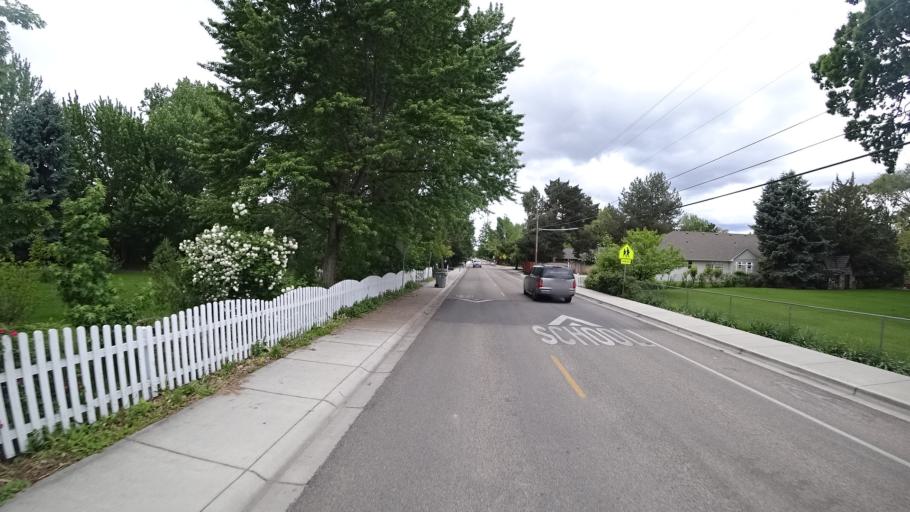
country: US
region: Idaho
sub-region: Ada County
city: Garden City
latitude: 43.6555
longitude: -116.2382
